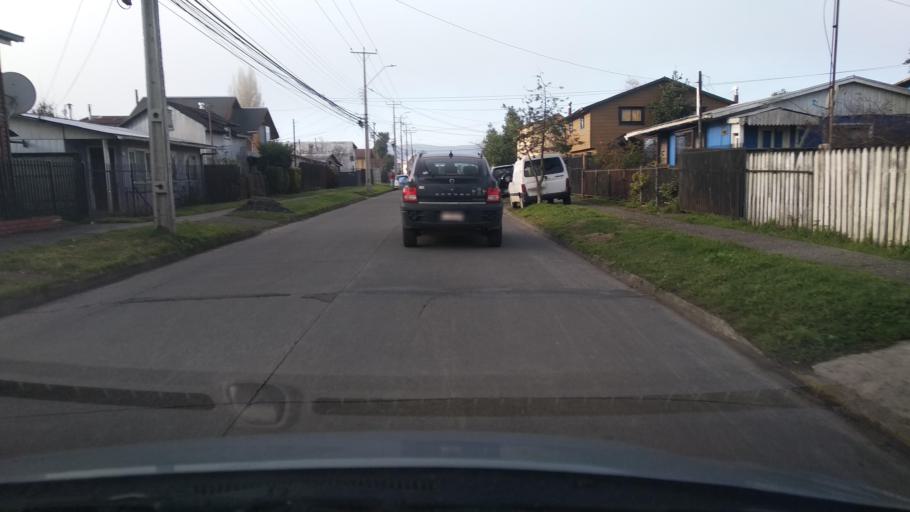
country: CL
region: Los Lagos
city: Las Animas
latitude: -39.8097
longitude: -73.2259
